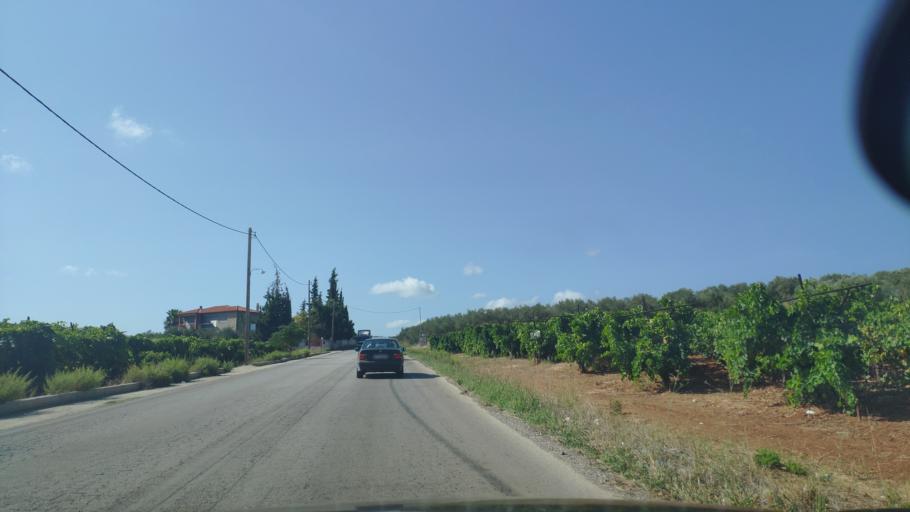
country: GR
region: Peloponnese
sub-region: Nomos Korinthias
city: Moulki
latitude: 37.9936
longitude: 22.7006
